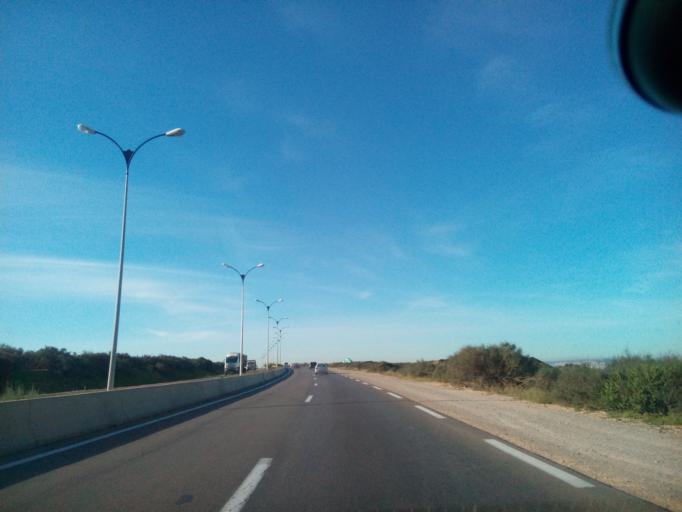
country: DZ
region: Oran
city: Ain el Bya
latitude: 35.7976
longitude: -0.0869
